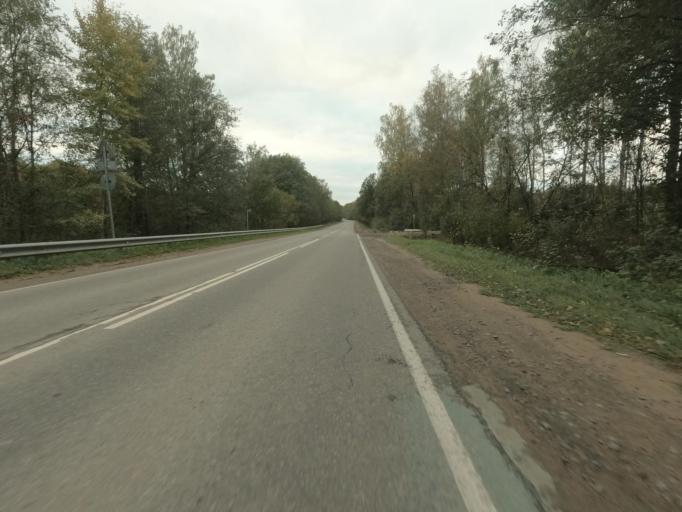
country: RU
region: Leningrad
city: Pavlovo
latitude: 59.7932
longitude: 30.9564
